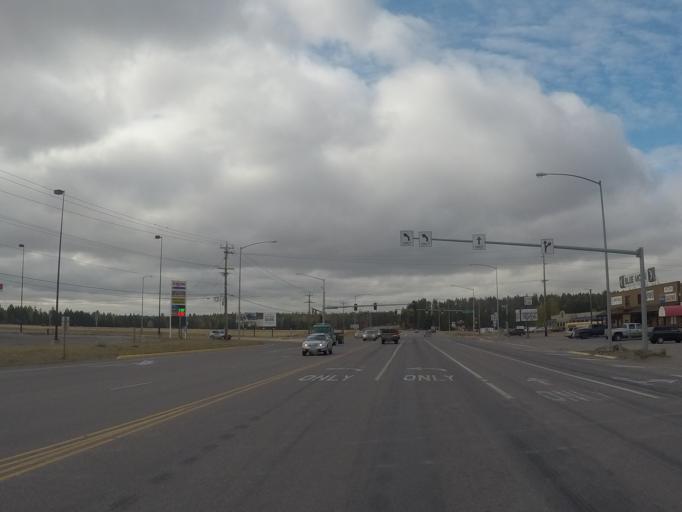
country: US
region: Montana
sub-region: Flathead County
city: Columbia Falls
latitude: 48.3707
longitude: -114.2392
